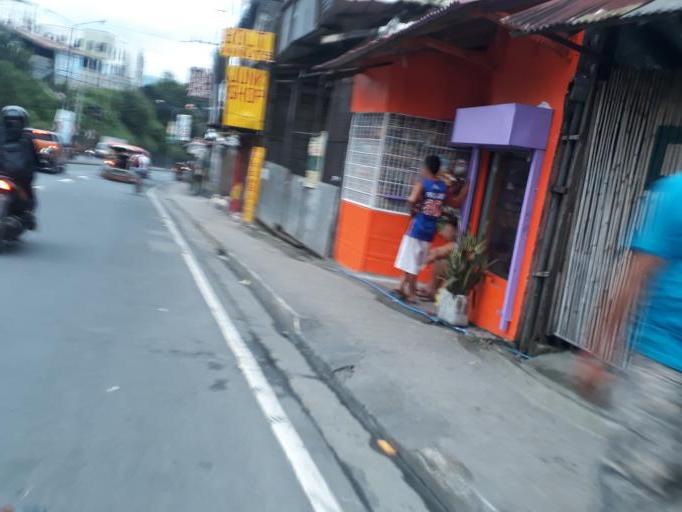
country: PH
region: Calabarzon
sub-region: Province of Rizal
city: San Mateo
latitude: 14.6873
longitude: 121.1001
